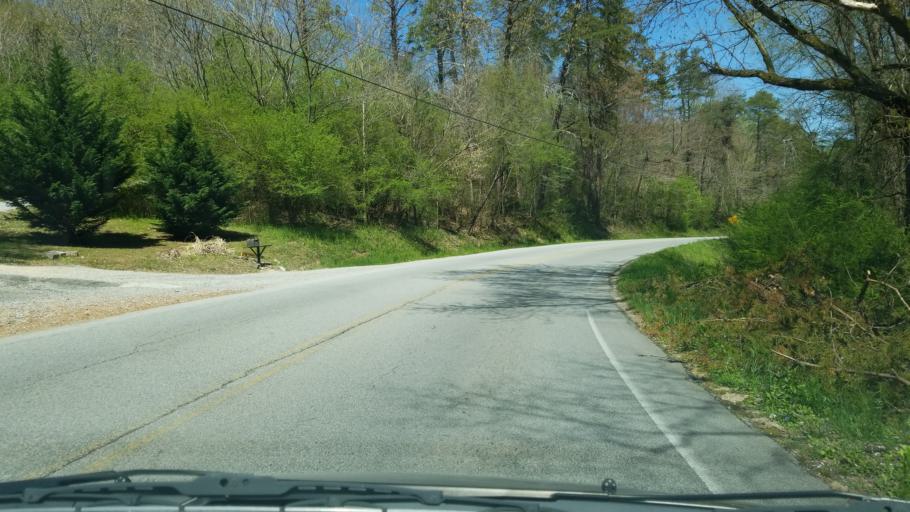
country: US
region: Tennessee
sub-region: Hamilton County
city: Middle Valley
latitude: 35.2071
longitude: -85.2136
